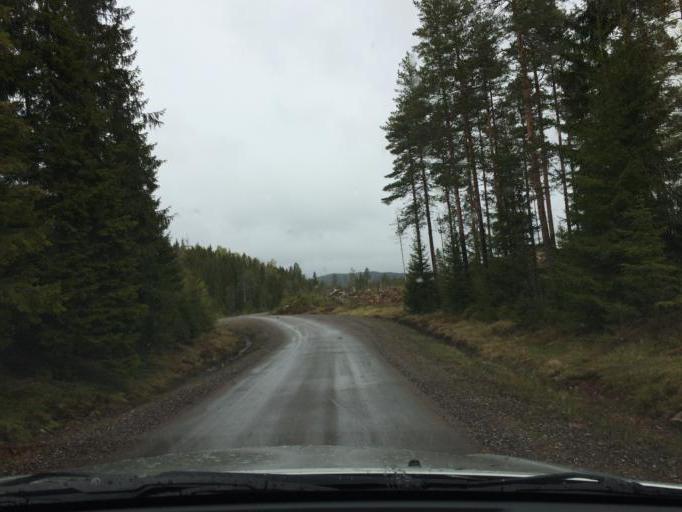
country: SE
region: OErebro
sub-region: Hallefors Kommun
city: Haellefors
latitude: 60.0153
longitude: 14.5941
